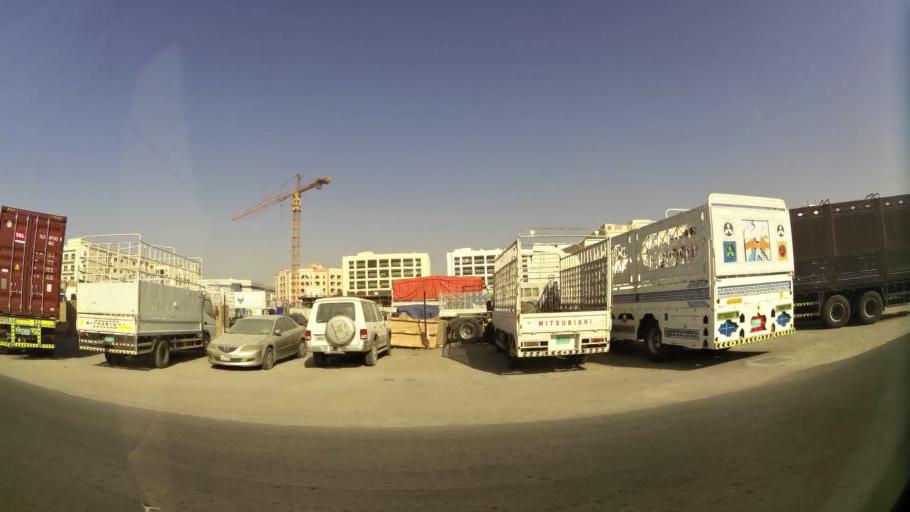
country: AE
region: Ash Shariqah
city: Sharjah
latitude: 25.2808
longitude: 55.3847
